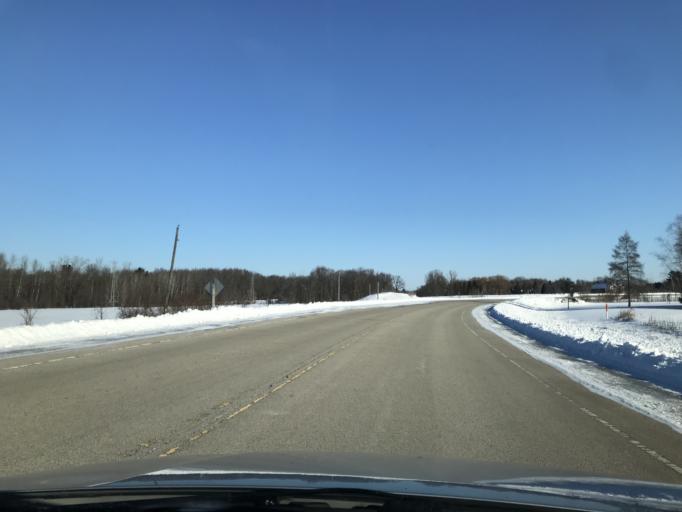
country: US
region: Wisconsin
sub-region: Oconto County
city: Oconto Falls
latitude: 44.9677
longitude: -88.0460
